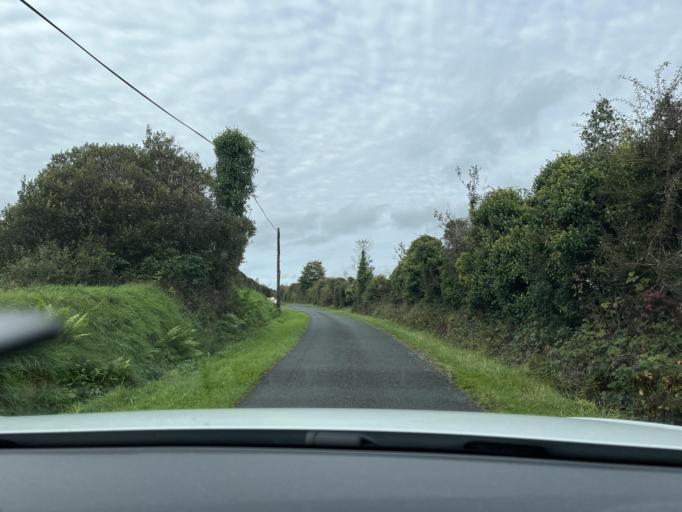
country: IE
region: Connaught
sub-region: Roscommon
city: Boyle
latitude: 54.0006
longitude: -8.2799
